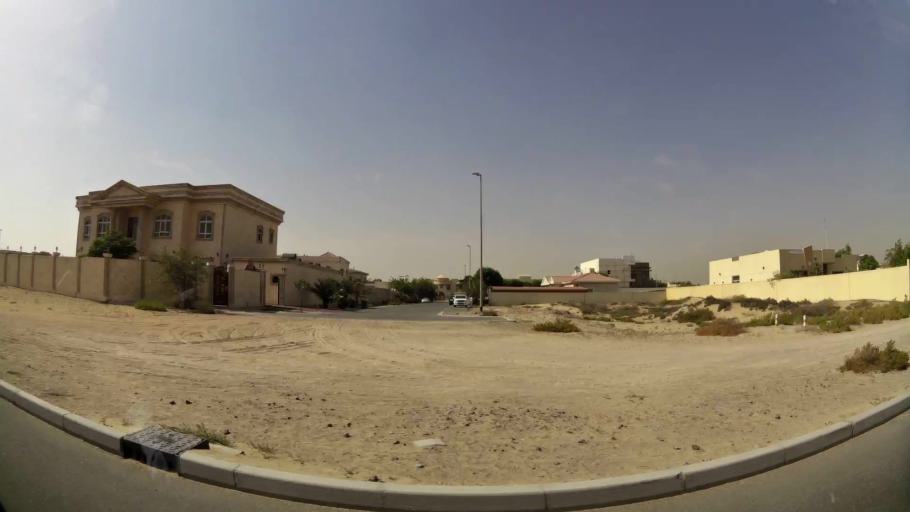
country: AE
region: Ash Shariqah
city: Sharjah
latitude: 25.2548
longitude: 55.4285
